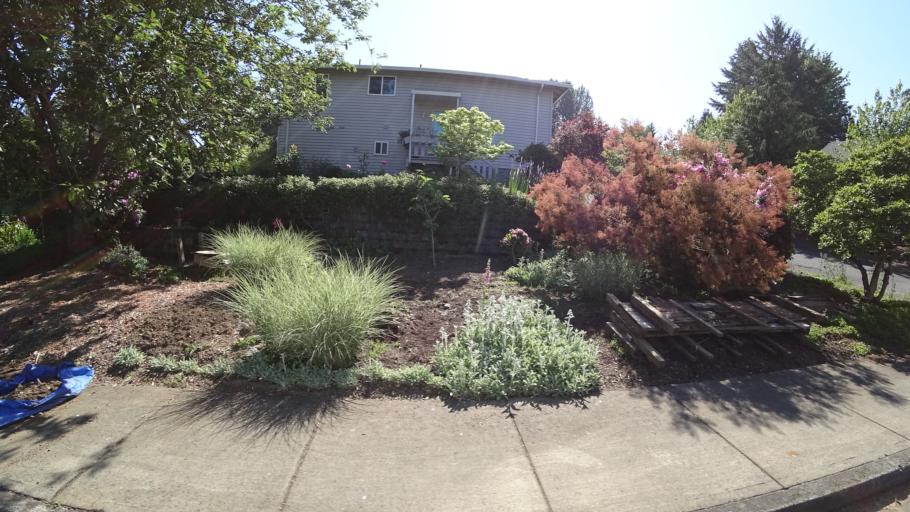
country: US
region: Oregon
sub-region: Multnomah County
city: Lents
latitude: 45.4678
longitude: -122.5628
